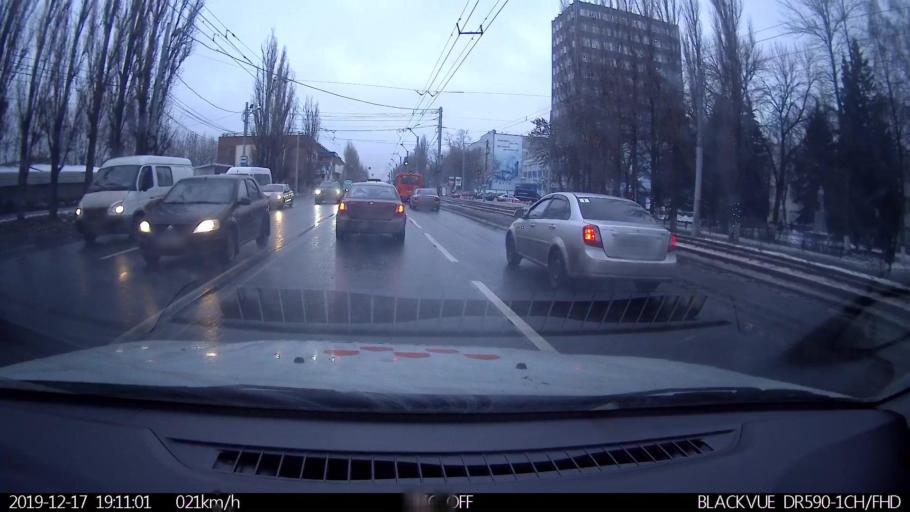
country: RU
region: Nizjnij Novgorod
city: Nizhniy Novgorod
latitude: 56.3338
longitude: 43.8926
